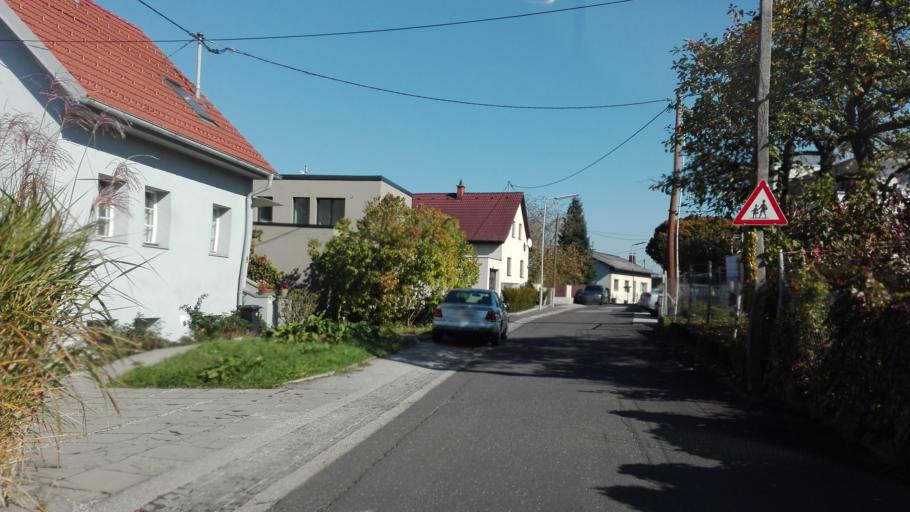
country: AT
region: Upper Austria
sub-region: Politischer Bezirk Linz-Land
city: Leonding
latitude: 48.2827
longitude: 14.2697
